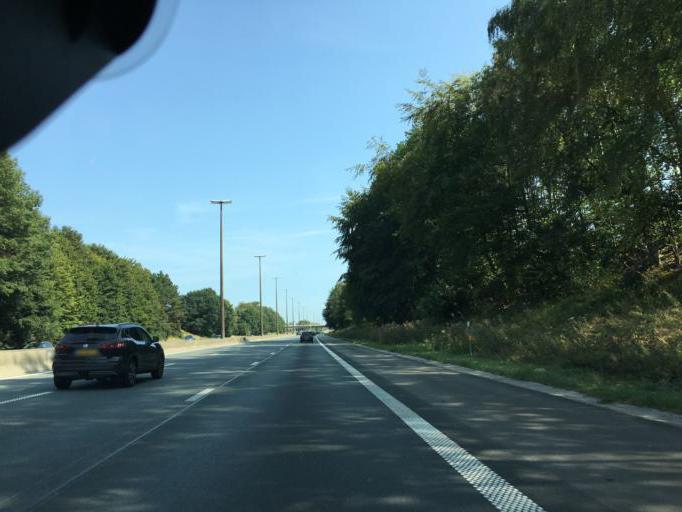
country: BE
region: Wallonia
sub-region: Province du Hainaut
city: Brunehault
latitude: 50.4788
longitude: 4.4695
